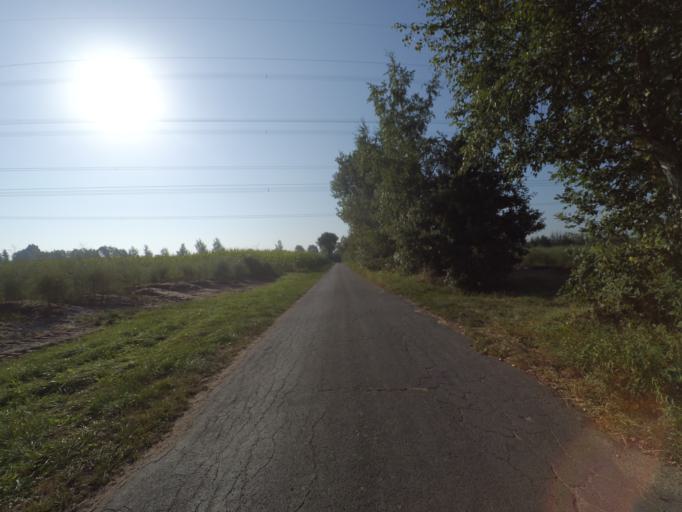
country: DE
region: Lower Saxony
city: Ohne
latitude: 52.2626
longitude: 7.2733
